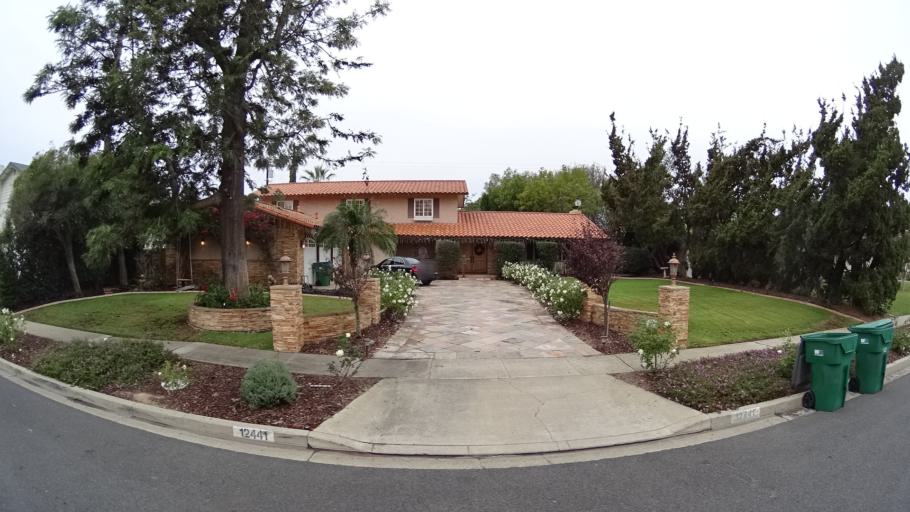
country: US
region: California
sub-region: Orange County
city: North Tustin
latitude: 33.7493
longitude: -117.7963
